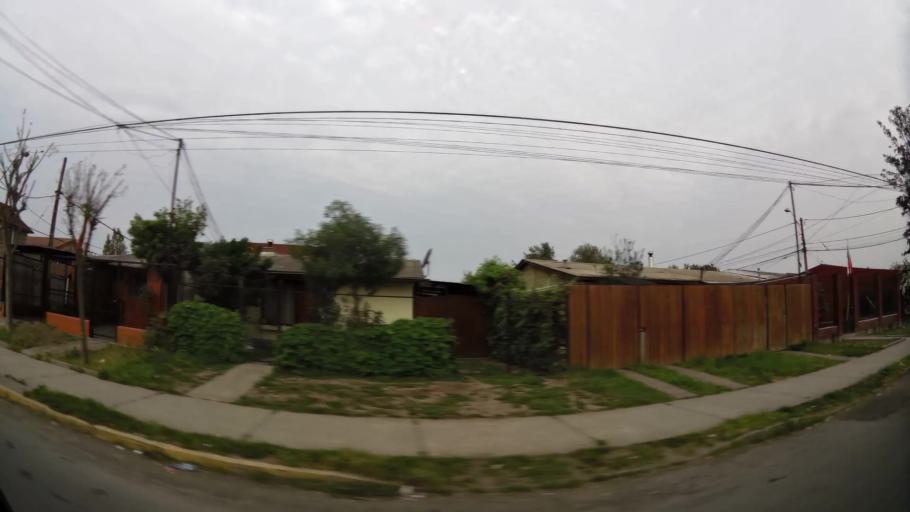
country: CL
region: Santiago Metropolitan
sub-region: Provincia de Santiago
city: Lo Prado
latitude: -33.5233
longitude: -70.7867
